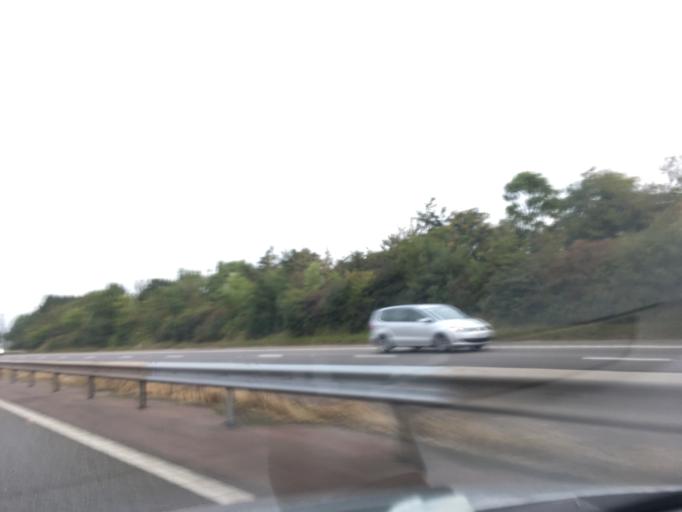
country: GB
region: England
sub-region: Oxfordshire
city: Somerton
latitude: 51.9613
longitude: -1.2212
